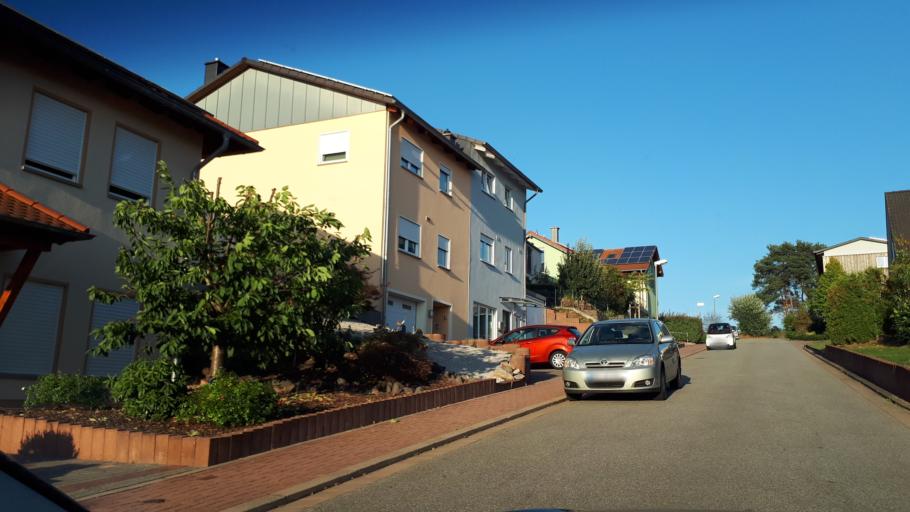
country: DE
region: Saarland
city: Eppelborn
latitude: 49.4212
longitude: 7.0129
